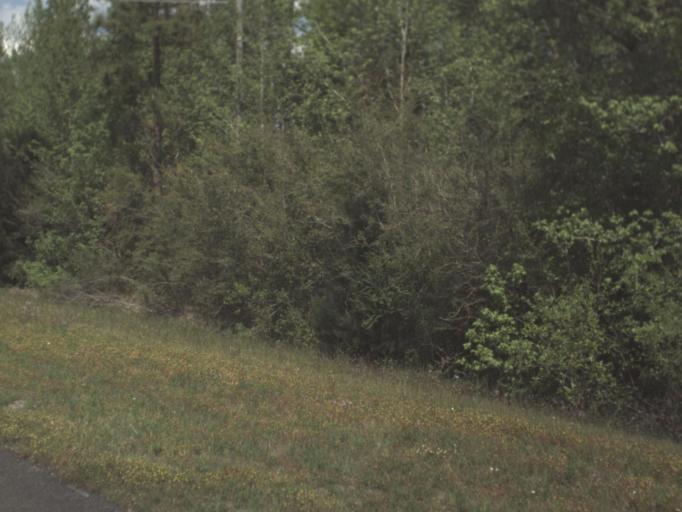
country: US
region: Florida
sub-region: Escambia County
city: Molino
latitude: 30.7842
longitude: -87.3353
